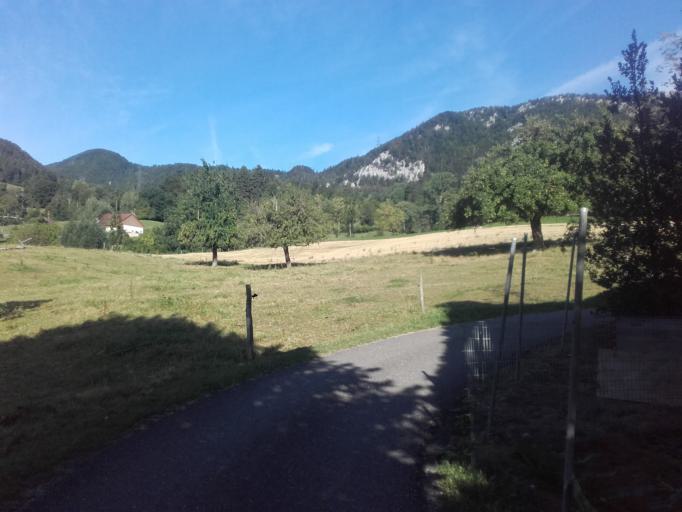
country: CH
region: Solothurn
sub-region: Bezirk Thal
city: Matzendorf
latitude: 47.3078
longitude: 7.5981
